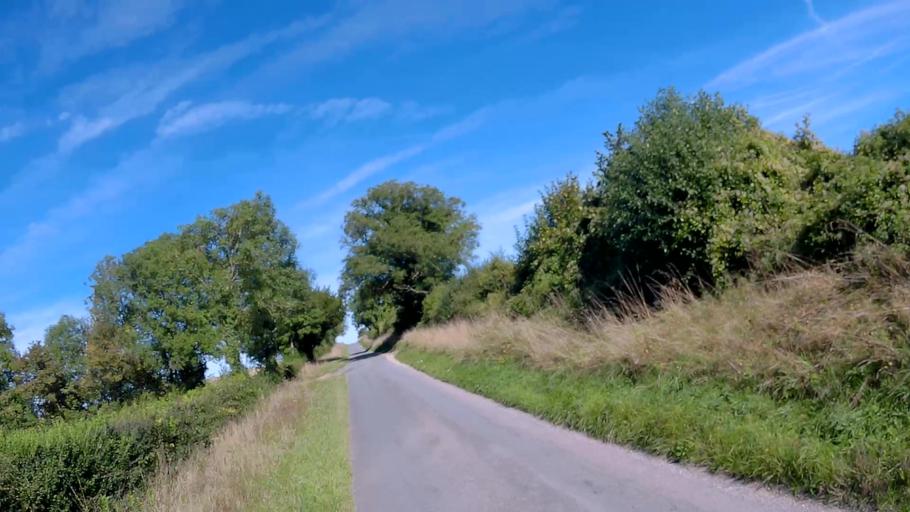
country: GB
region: England
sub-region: Hampshire
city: Andover
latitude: 51.1655
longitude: -1.3960
